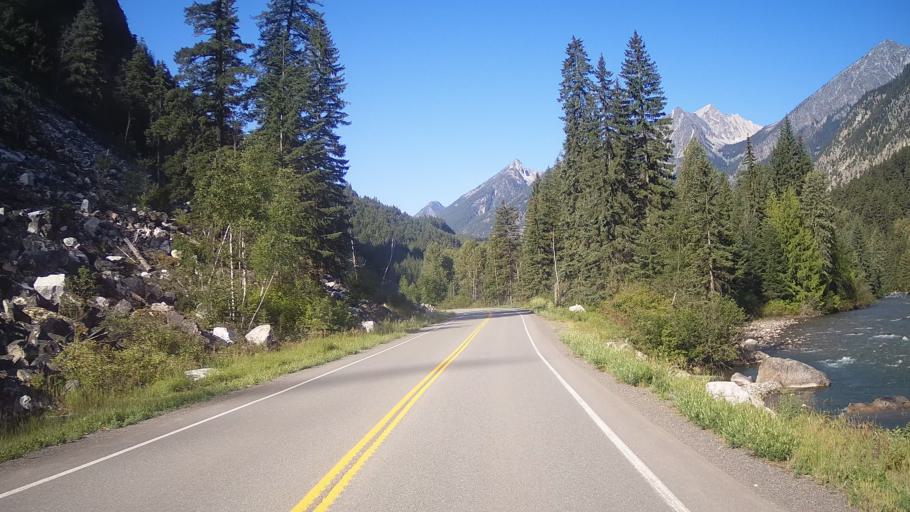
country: CA
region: British Columbia
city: Lillooet
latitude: 50.5406
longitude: -122.1128
